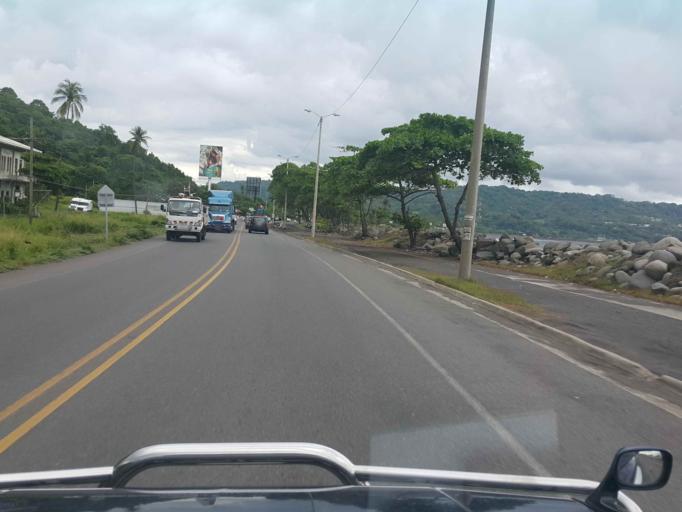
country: CR
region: Puntarenas
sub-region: Canton Central de Puntarenas
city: Chacarita
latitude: 9.9328
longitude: -84.7218
